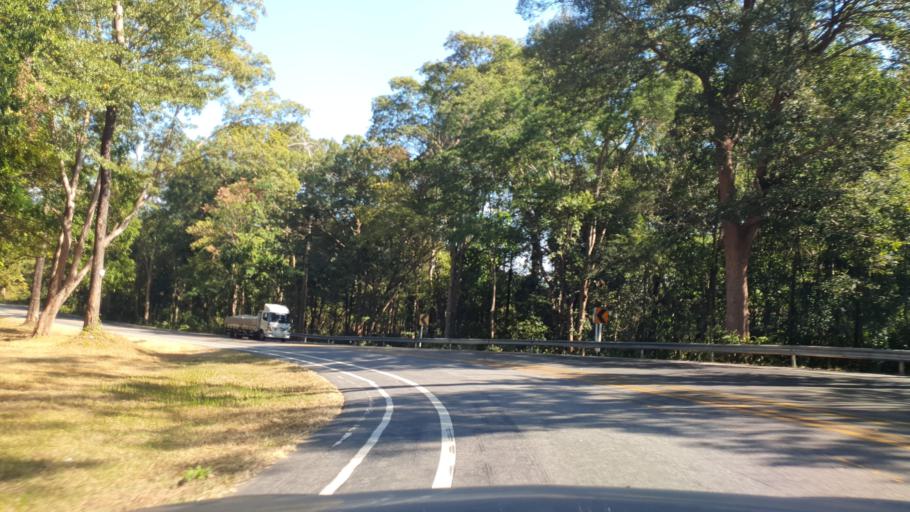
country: TH
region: Kalasin
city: Na Khu
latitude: 16.8414
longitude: 103.9108
